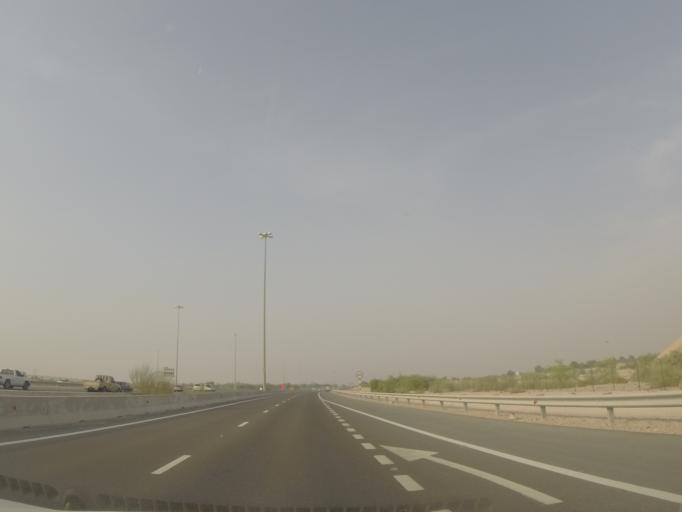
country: AE
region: Abu Dhabi
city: Abu Dhabi
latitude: 24.6997
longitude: 54.7840
